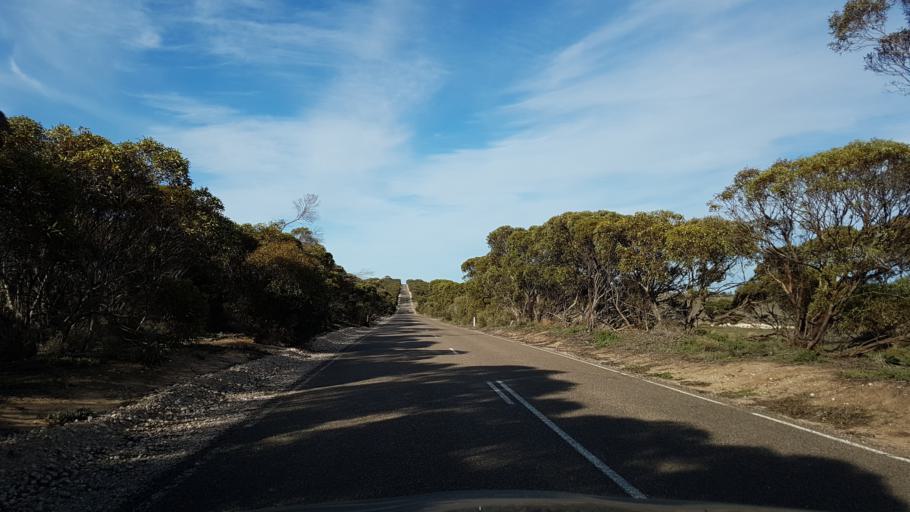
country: AU
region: South Australia
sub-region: Murray Bridge
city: Tailem Bend
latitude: -35.0637
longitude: 139.4655
